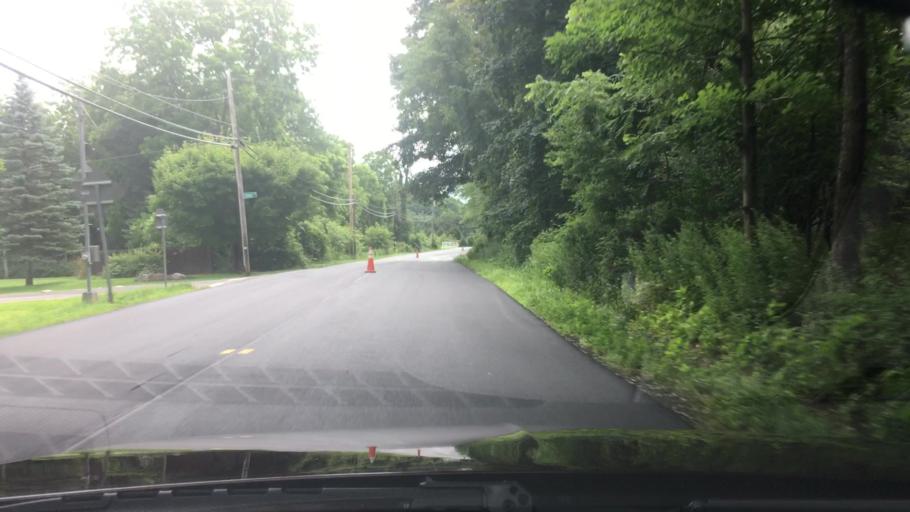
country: US
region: New York
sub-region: Dutchess County
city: Hillside Lake
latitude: 41.5793
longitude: -73.7435
